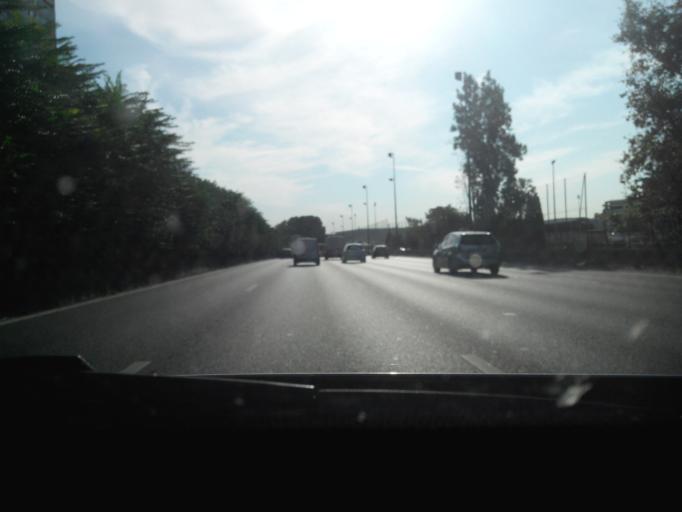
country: FR
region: Ile-de-France
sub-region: Departement du Val-de-Marne
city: Charenton-le-Pont
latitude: 48.8187
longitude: 2.4084
